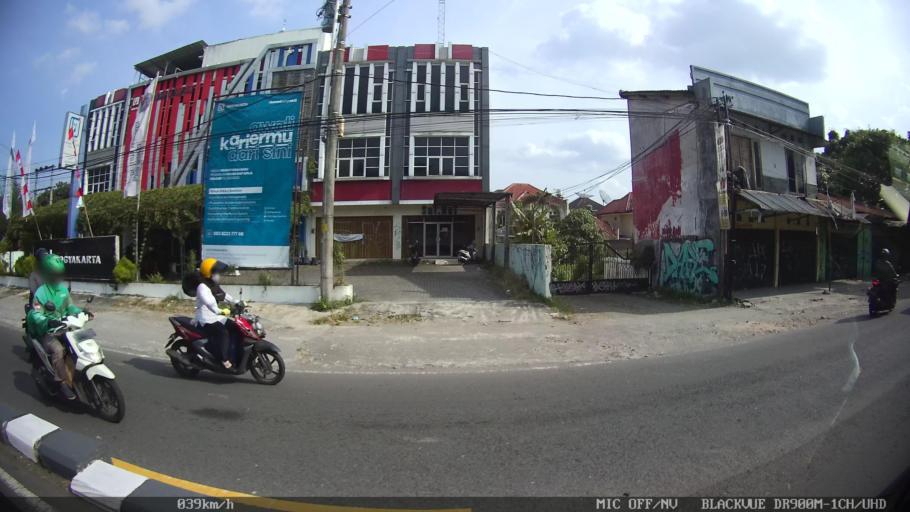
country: ID
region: Daerah Istimewa Yogyakarta
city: Melati
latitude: -7.7516
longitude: 110.3744
